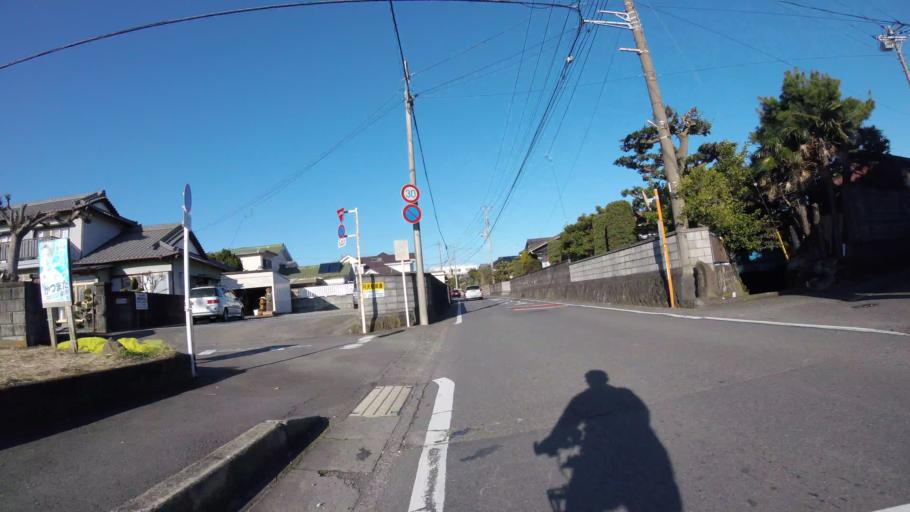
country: JP
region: Shizuoka
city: Numazu
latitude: 35.1123
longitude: 138.8701
